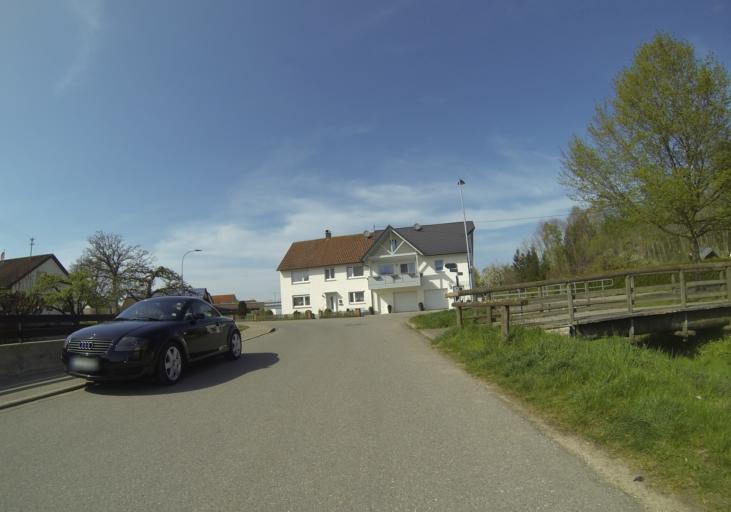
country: DE
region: Baden-Wuerttemberg
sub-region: Tuebingen Region
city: Huttisheim
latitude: 48.2761
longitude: 9.9459
